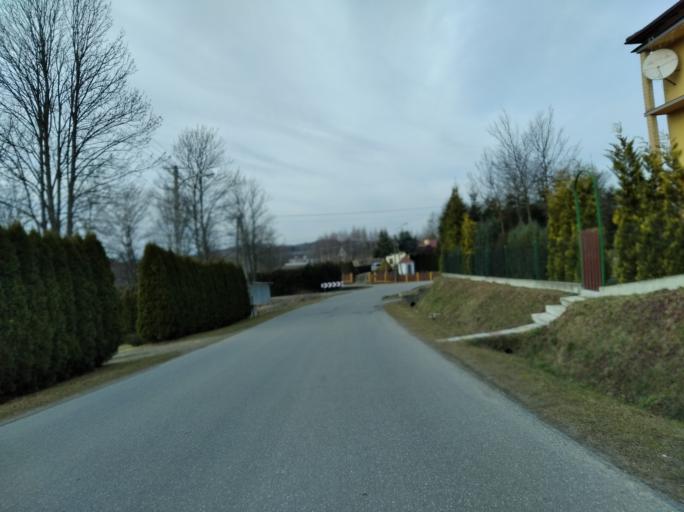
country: PL
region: Subcarpathian Voivodeship
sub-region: Powiat brzozowski
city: Gorki
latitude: 49.6515
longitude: 22.0326
